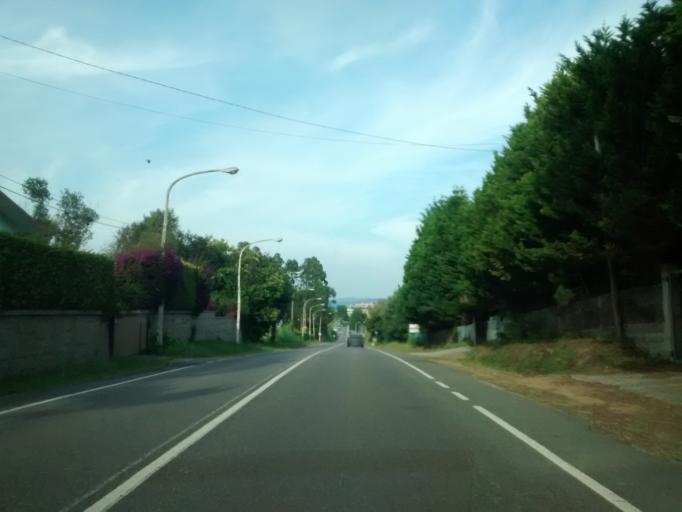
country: ES
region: Galicia
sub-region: Provincia de Pontevedra
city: Sanxenxo
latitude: 42.3920
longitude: -8.8384
